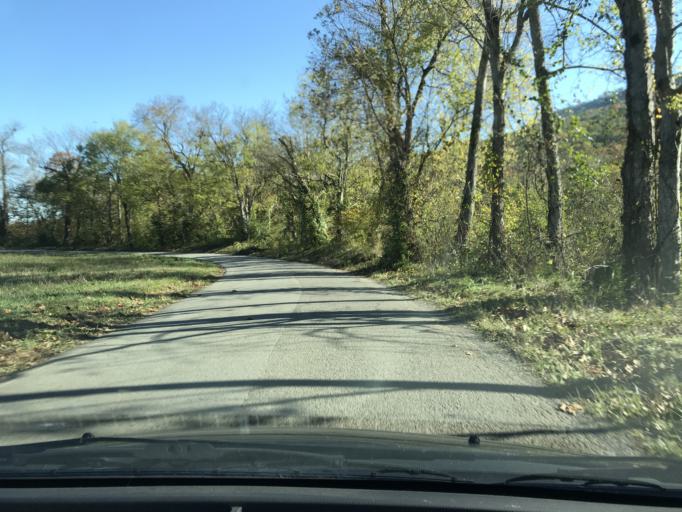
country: US
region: Georgia
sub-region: Dade County
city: Trenton
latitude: 34.8983
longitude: -85.4622
